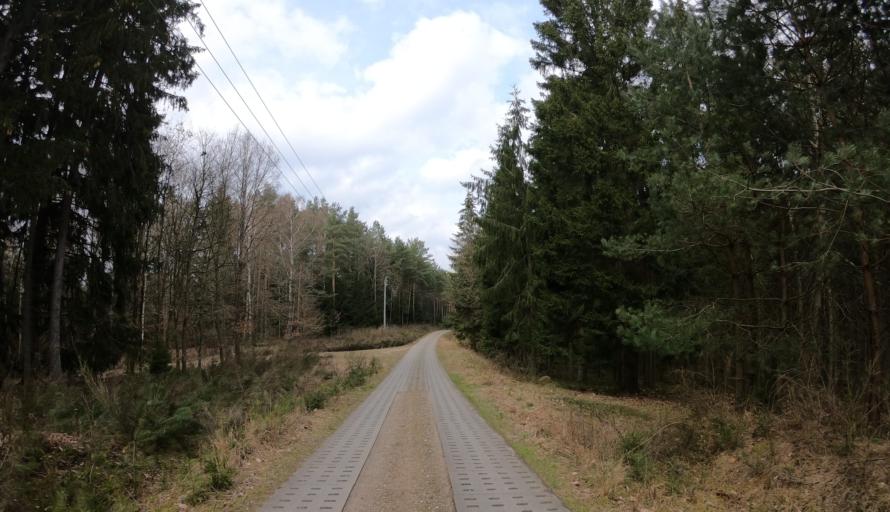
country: PL
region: West Pomeranian Voivodeship
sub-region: Powiat swidwinski
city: Rabino
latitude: 53.8673
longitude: 15.8722
